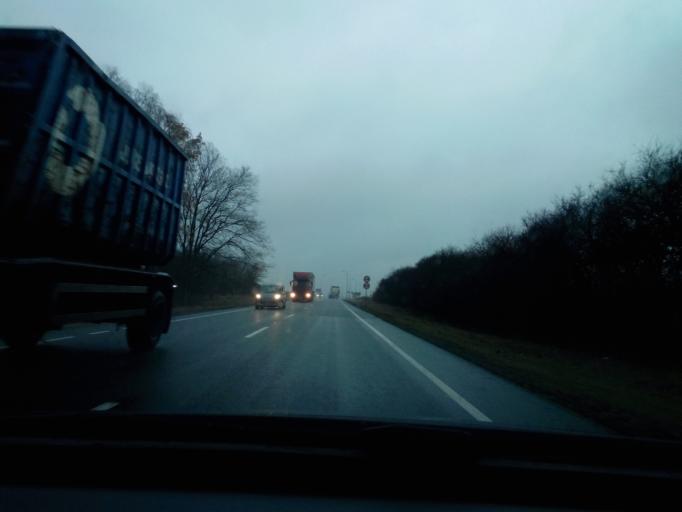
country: PL
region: Pomeranian Voivodeship
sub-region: Powiat tczewski
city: Subkowy
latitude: 54.0383
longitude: 18.6821
